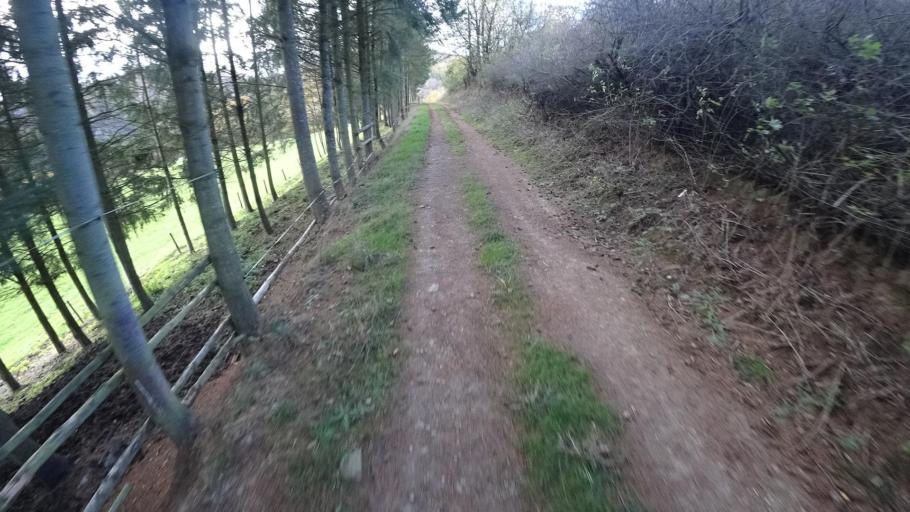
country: DE
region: Rheinland-Pfalz
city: Lind
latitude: 50.4859
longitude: 6.9134
